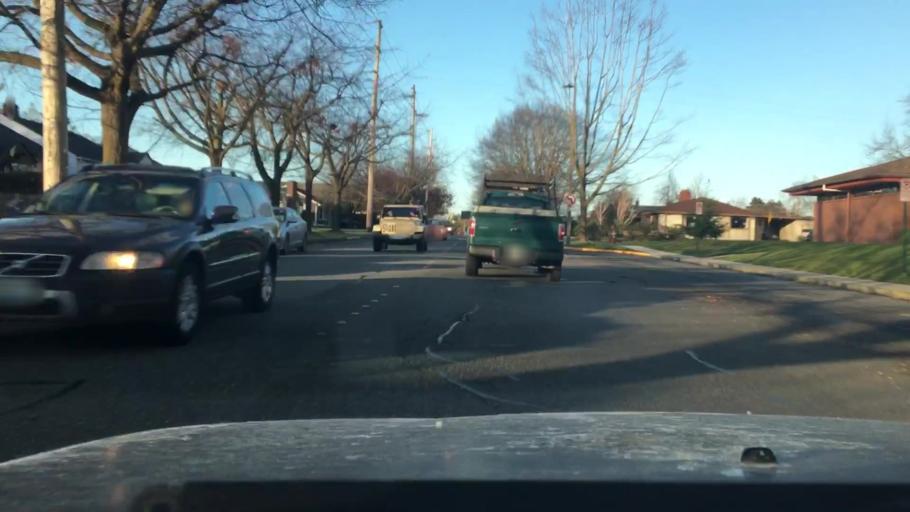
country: US
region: Washington
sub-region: Whatcom County
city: Bellingham
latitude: 48.7674
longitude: -122.4649
